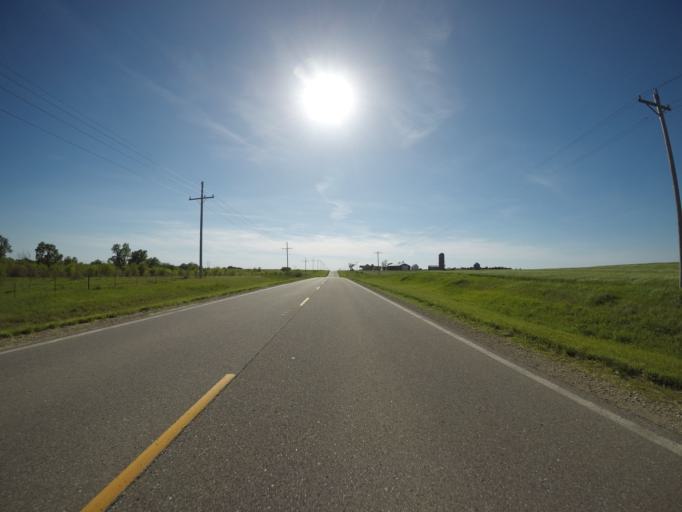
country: US
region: Kansas
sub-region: Clay County
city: Clay Center
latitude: 39.3646
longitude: -96.8996
